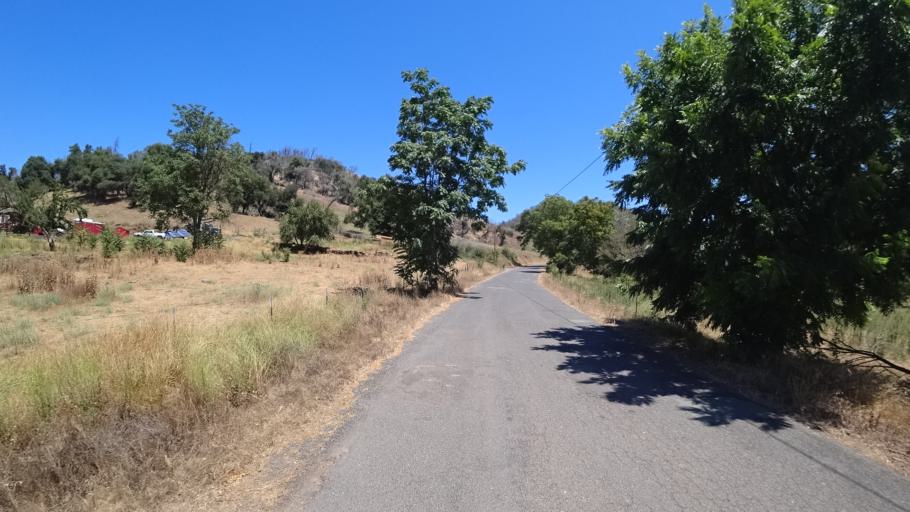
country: US
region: California
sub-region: Calaveras County
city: San Andreas
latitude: 38.2854
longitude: -120.6456
